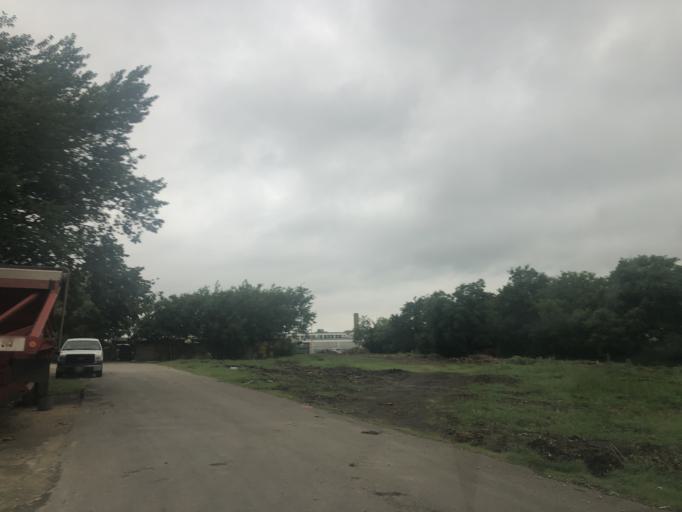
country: US
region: Texas
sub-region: Dallas County
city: Cockrell Hill
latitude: 32.7768
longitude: -96.8661
